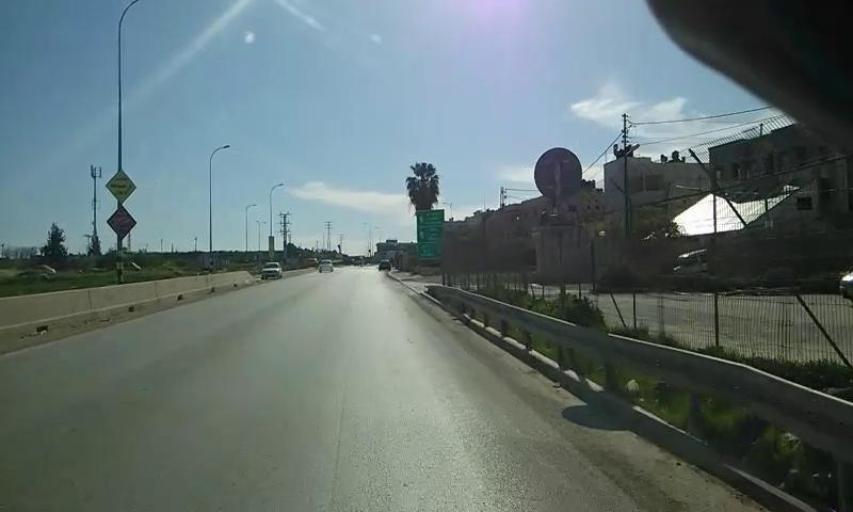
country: PS
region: West Bank
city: Ar Ram wa Dahiyat al Barid
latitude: 31.8569
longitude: 35.2387
